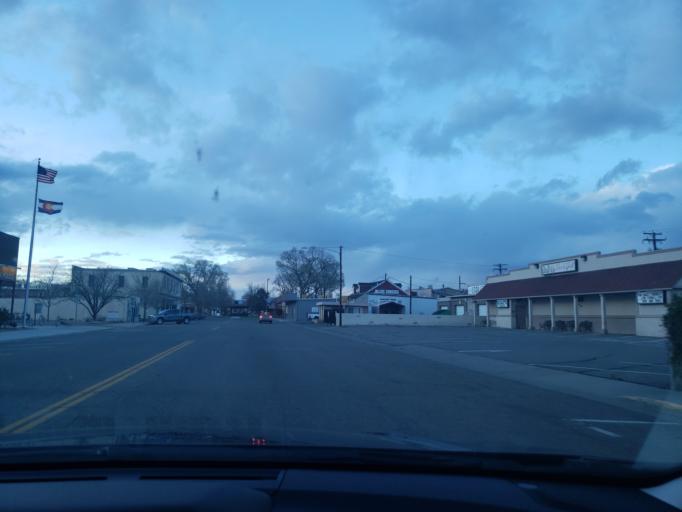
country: US
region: Colorado
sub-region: Mesa County
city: Fruita
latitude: 39.1572
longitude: -108.7336
